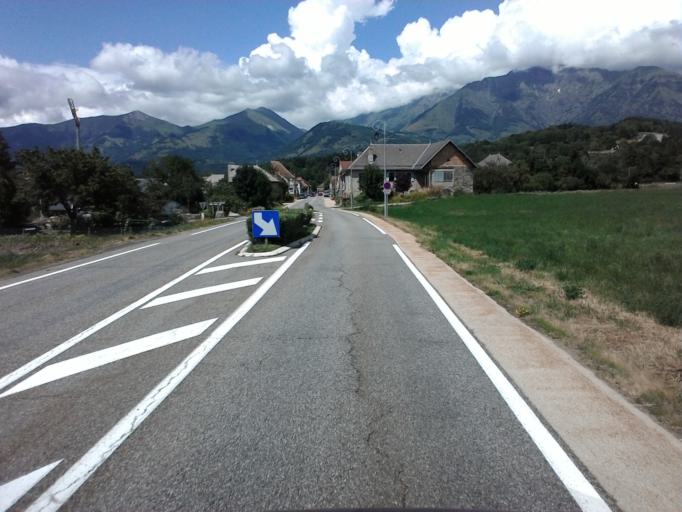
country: FR
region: Provence-Alpes-Cote d'Azur
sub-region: Departement des Hautes-Alpes
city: Saint-Bonnet-en-Champsaur
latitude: 44.7506
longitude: 6.0085
